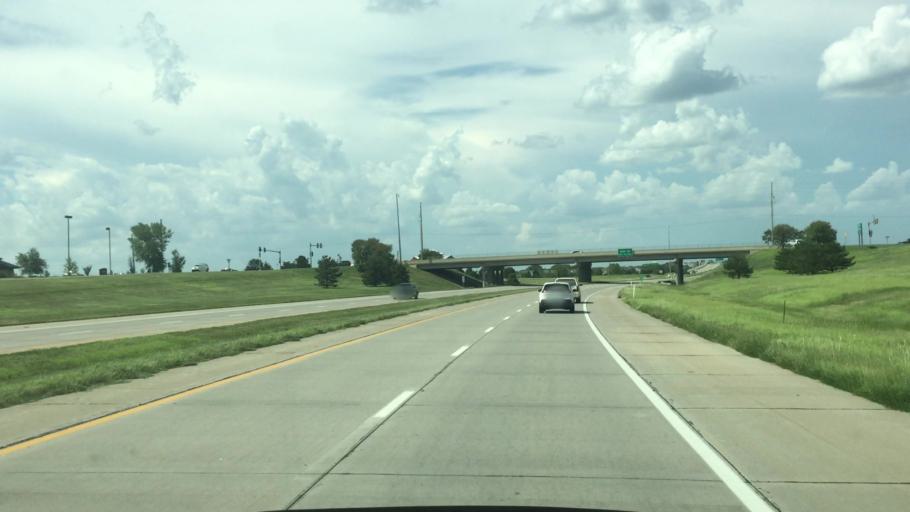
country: US
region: Kansas
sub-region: Butler County
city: Andover
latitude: 37.7065
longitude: -97.2002
